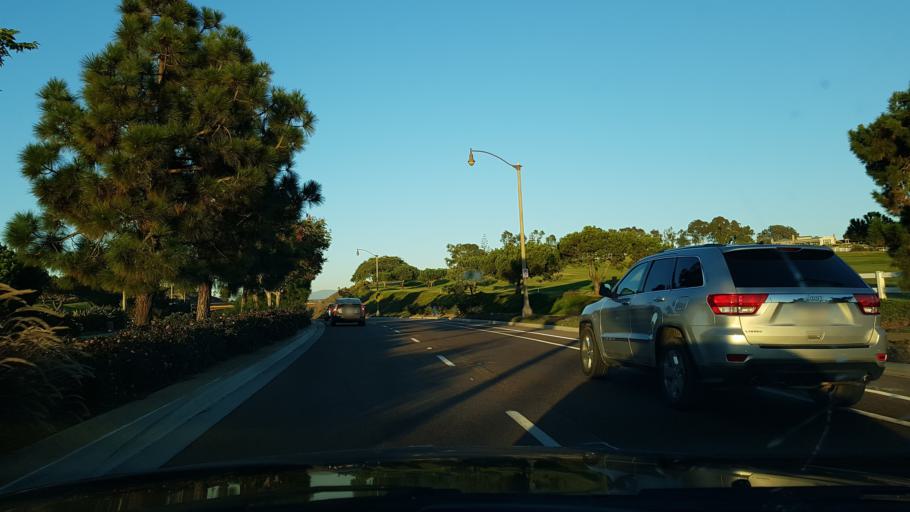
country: US
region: California
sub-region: San Diego County
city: Encinitas
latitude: 33.0660
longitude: -117.2764
